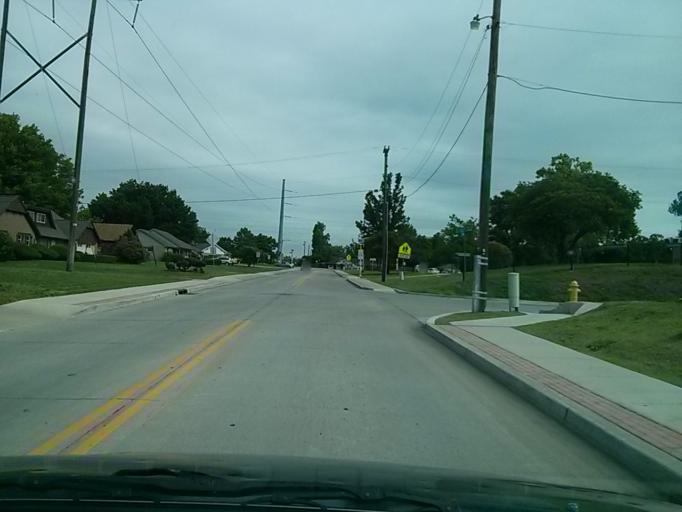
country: US
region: Oklahoma
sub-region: Tulsa County
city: Tulsa
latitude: 36.1099
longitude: -95.9133
